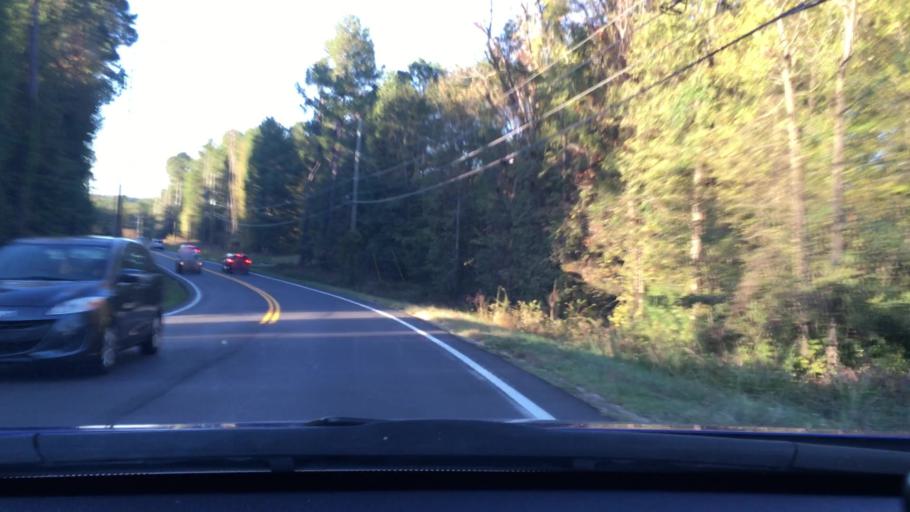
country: US
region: South Carolina
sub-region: Lexington County
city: Irmo
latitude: 34.1047
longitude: -81.1605
